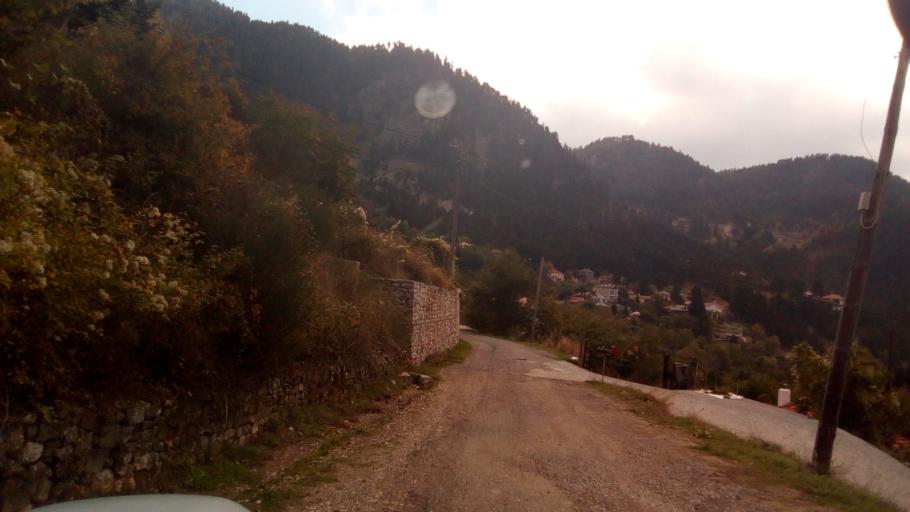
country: GR
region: West Greece
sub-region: Nomos Aitolias kai Akarnanias
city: Thermo
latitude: 38.6494
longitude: 21.9200
